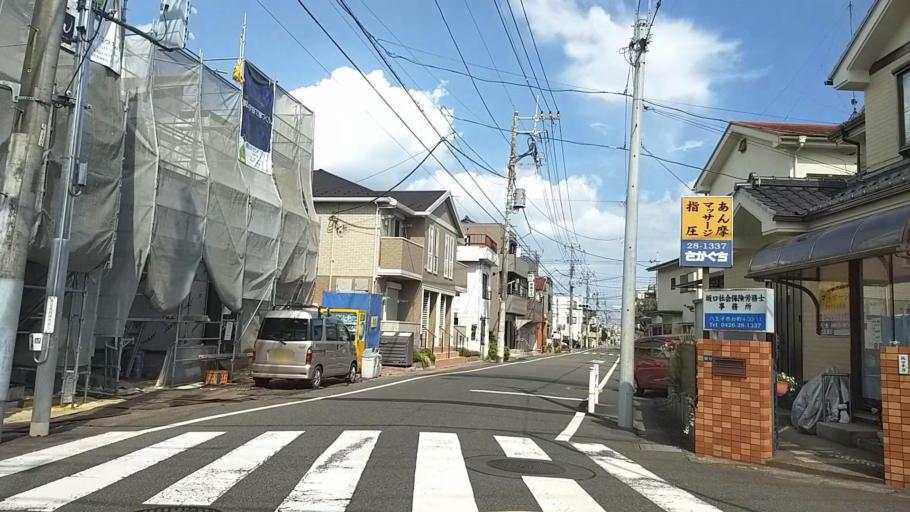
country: JP
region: Tokyo
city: Hachioji
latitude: 35.6580
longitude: 139.3187
